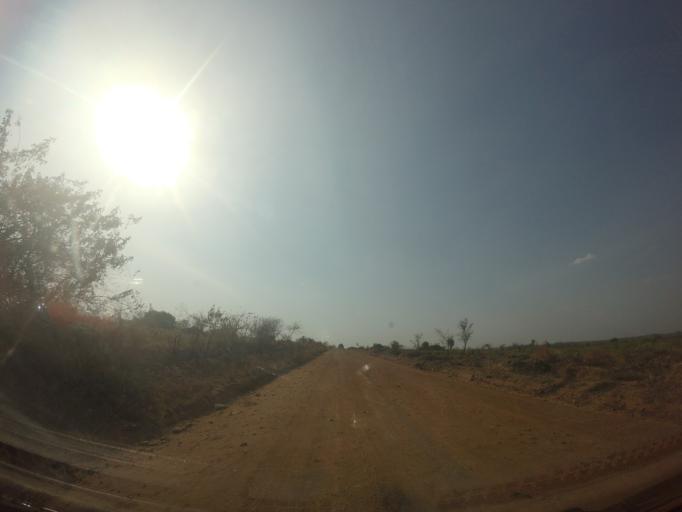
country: UG
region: Northern Region
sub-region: Maracha District
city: Maracha
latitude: 3.1041
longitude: 31.2098
